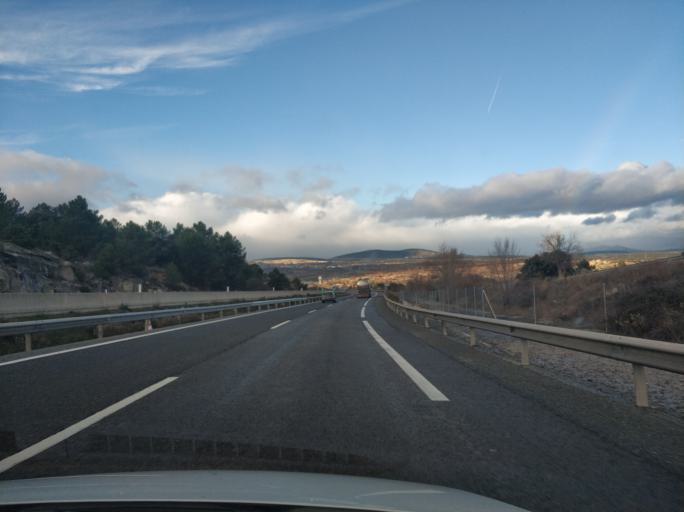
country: ES
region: Madrid
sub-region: Provincia de Madrid
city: La Cabrera
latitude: 40.8923
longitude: -3.6024
